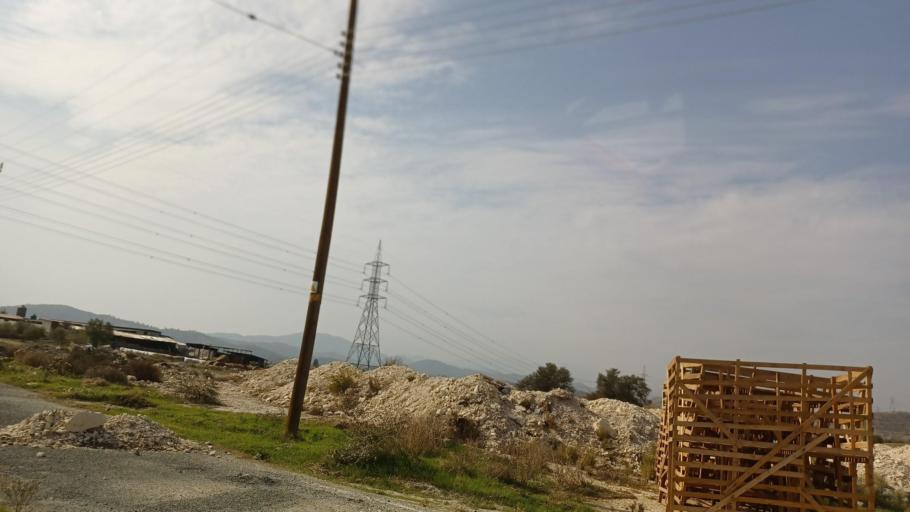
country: CY
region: Lefkosia
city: Lympia
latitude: 34.9834
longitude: 33.4535
